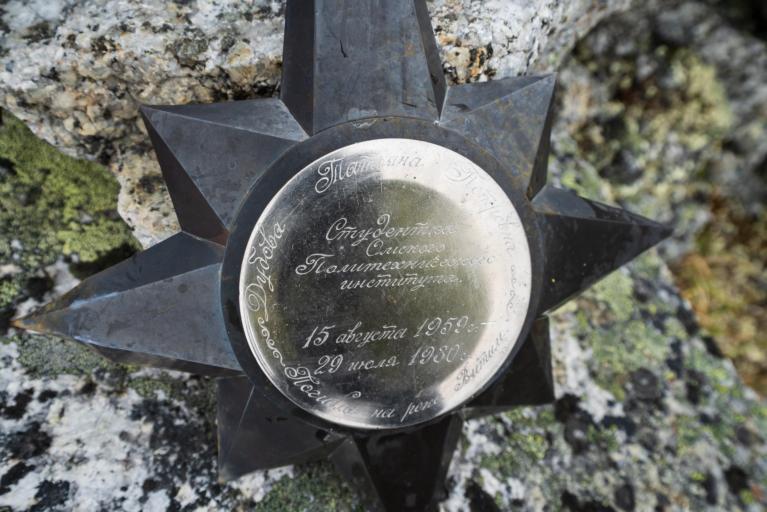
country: RU
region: Transbaikal Territory
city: Chara
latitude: 56.8685
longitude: 117.3859
